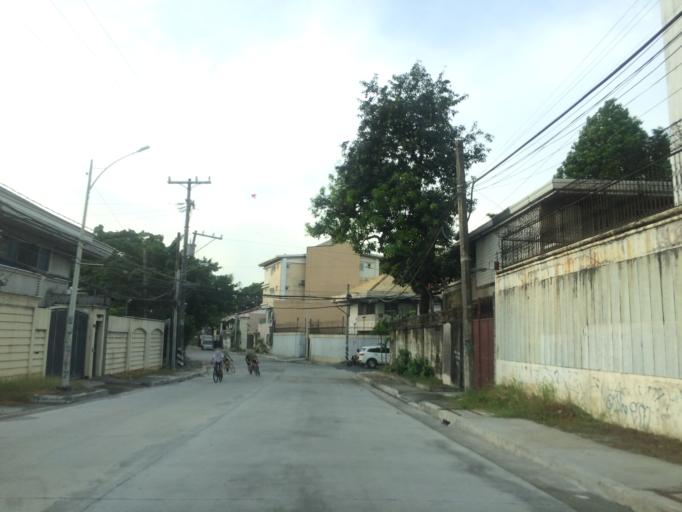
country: PH
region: Calabarzon
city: Del Monte
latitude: 14.6289
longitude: 121.0064
